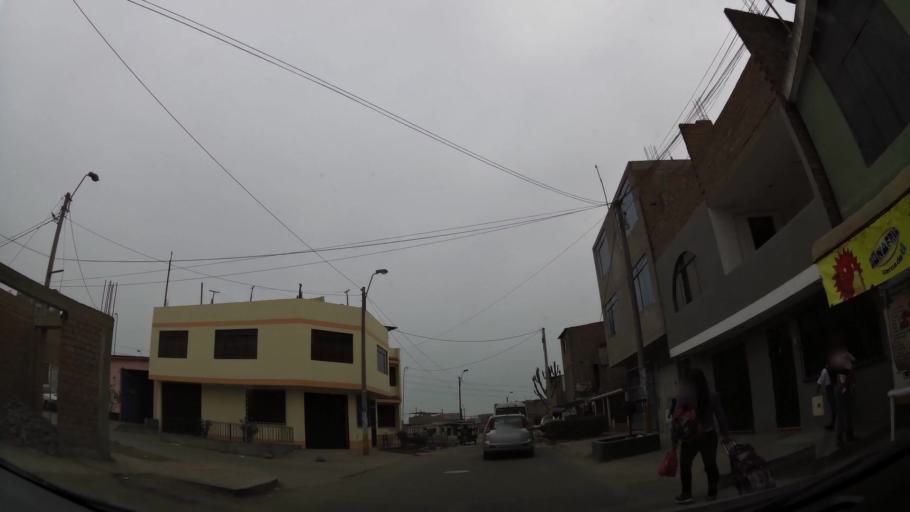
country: PE
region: Lima
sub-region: Lima
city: Surco
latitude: -12.1978
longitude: -76.9620
